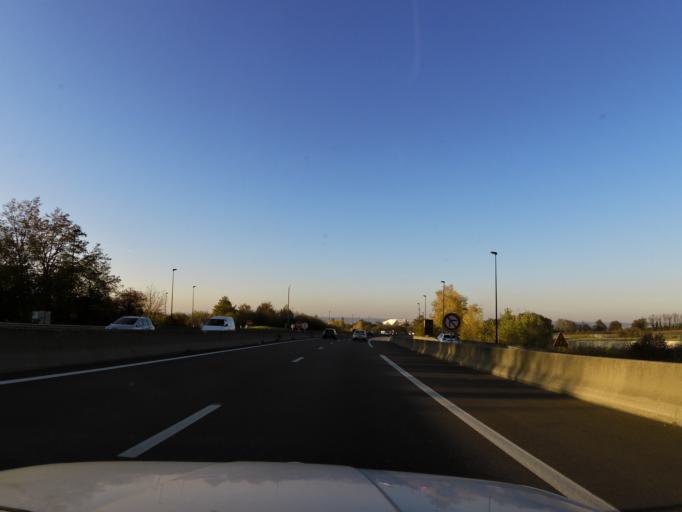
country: FR
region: Rhone-Alpes
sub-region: Departement du Rhone
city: Chassieu
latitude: 45.7505
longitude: 4.9866
